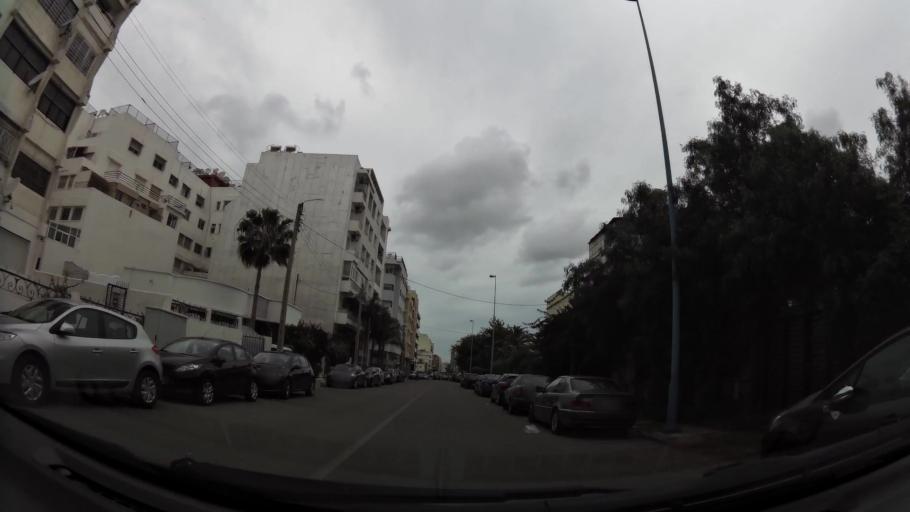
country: MA
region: Grand Casablanca
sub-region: Casablanca
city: Casablanca
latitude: 33.5678
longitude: -7.6248
